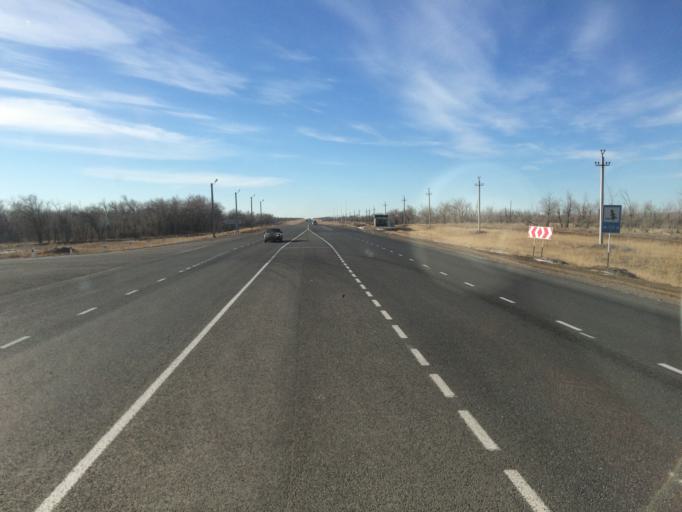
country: KZ
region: Aqtoebe
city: Aqtobe
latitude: 50.2642
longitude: 56.9535
